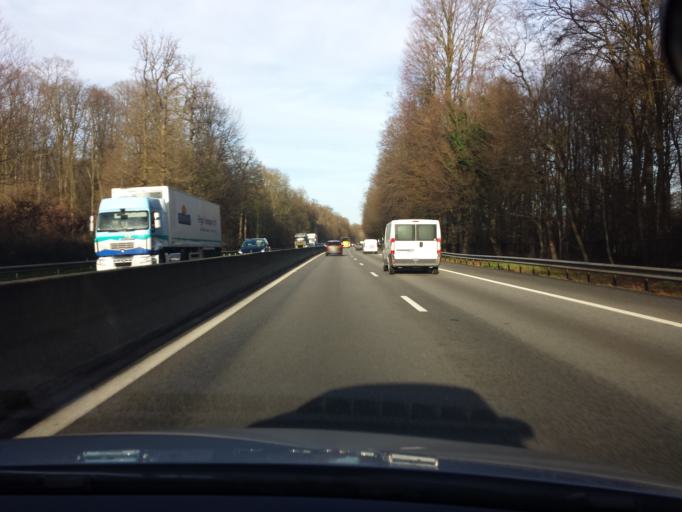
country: FR
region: Ile-de-France
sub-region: Departement des Yvelines
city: Saint-Nom-la-Breteche
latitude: 48.8801
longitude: 2.0173
